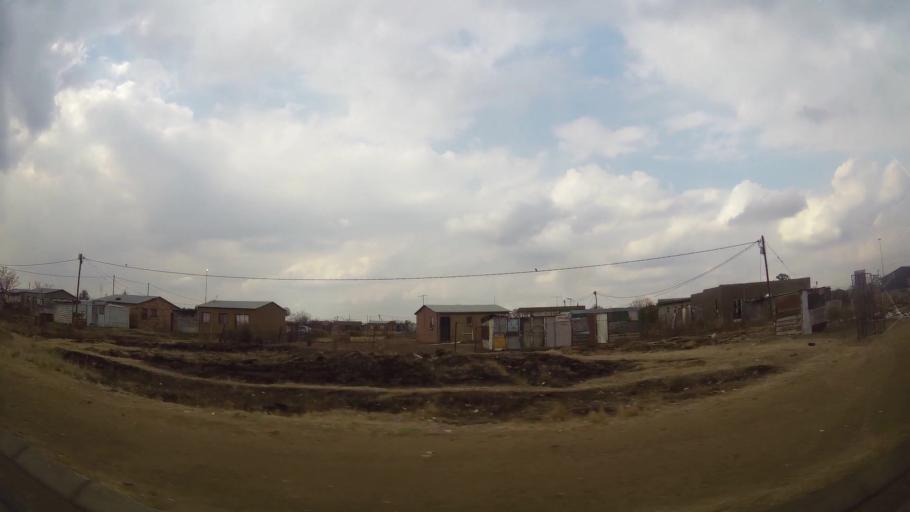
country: ZA
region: Orange Free State
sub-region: Fezile Dabi District Municipality
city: Sasolburg
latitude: -26.8621
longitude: 27.8731
